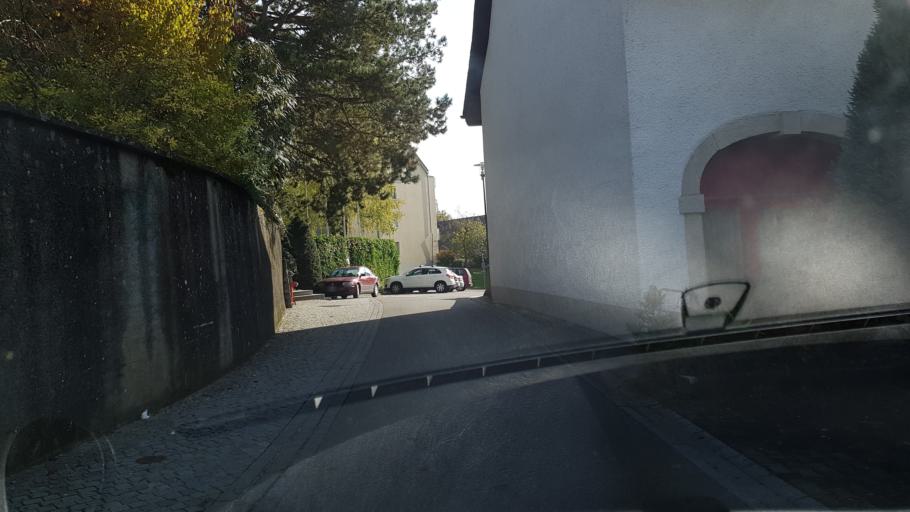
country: CH
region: Aargau
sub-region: Bezirk Baden
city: Birmenstorf
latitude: 47.4621
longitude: 8.2482
